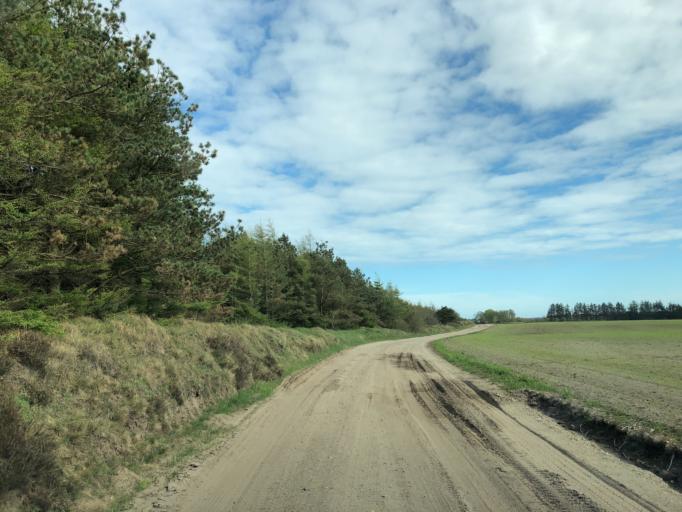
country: DK
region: Central Jutland
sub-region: Holstebro Kommune
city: Ulfborg
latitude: 56.2466
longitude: 8.3389
